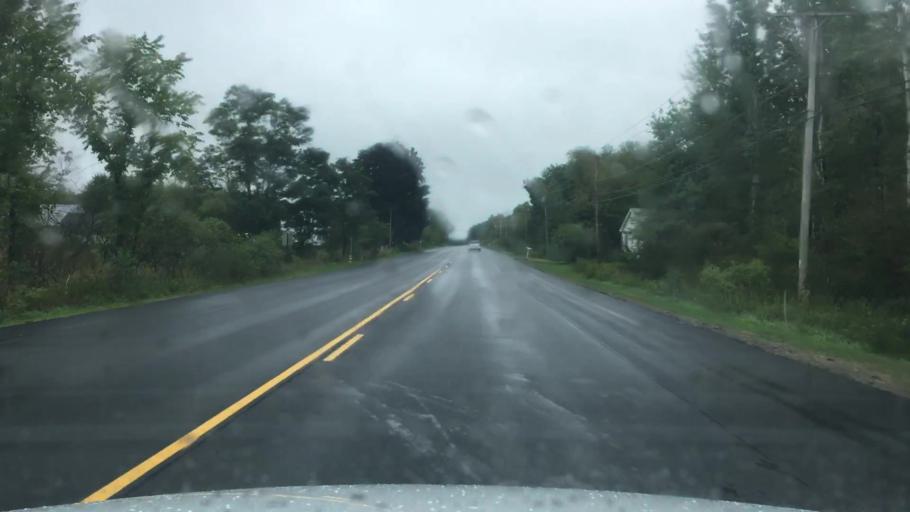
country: US
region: Maine
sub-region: Penobscot County
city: Hampden
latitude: 44.7606
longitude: -68.8475
